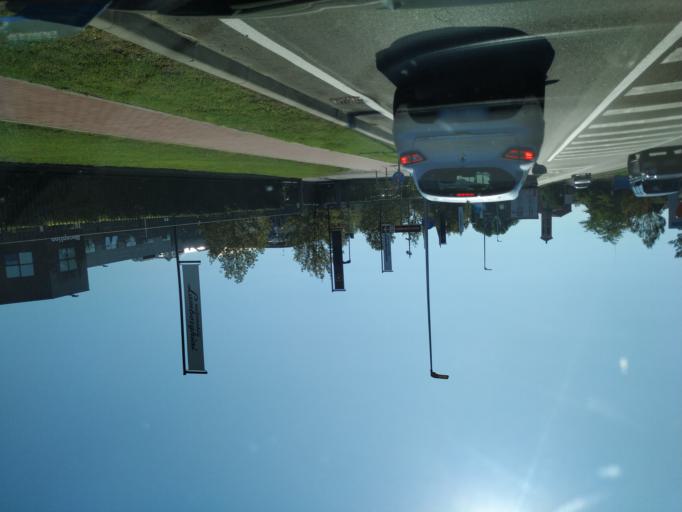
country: IT
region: Emilia-Romagna
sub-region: Provincia di Bologna
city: Sant'Agata Bolognese
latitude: 44.6597
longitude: 11.1259
